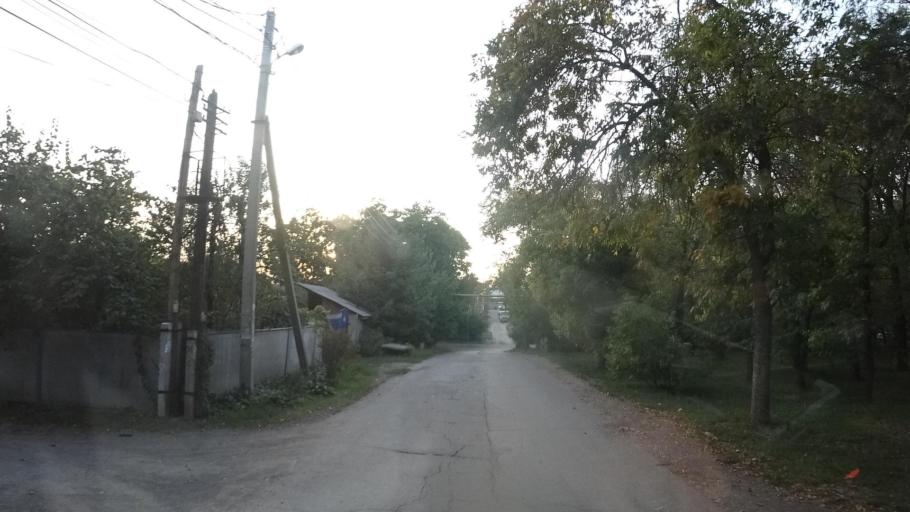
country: KZ
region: Almaty Oblysy
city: Pervomayskiy
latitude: 43.3356
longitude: 76.9939
